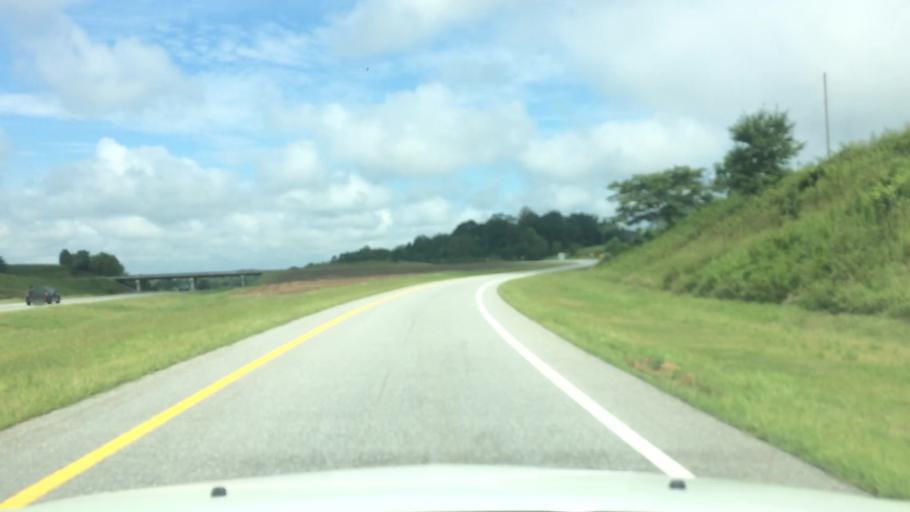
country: US
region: North Carolina
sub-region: Yadkin County
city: Jonesville
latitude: 36.1296
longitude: -80.8384
